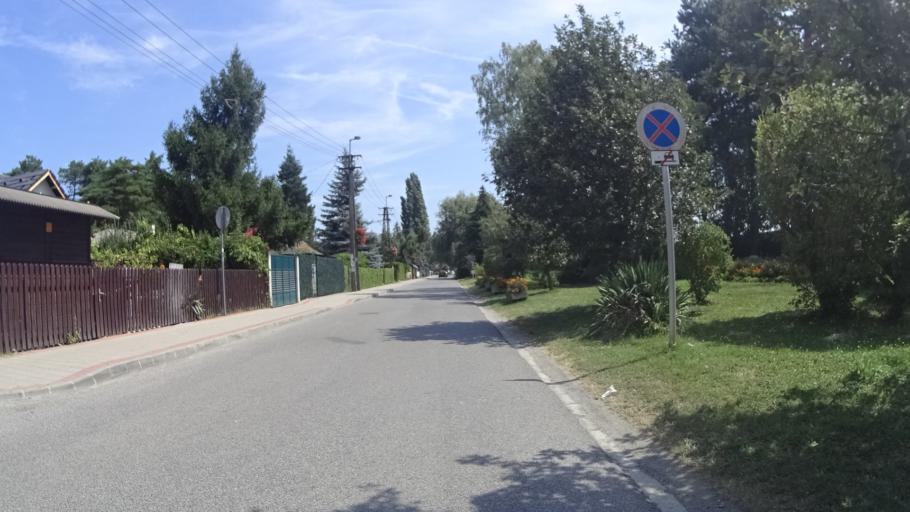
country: HU
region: Somogy
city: Balatonfenyves
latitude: 46.7141
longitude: 17.4843
